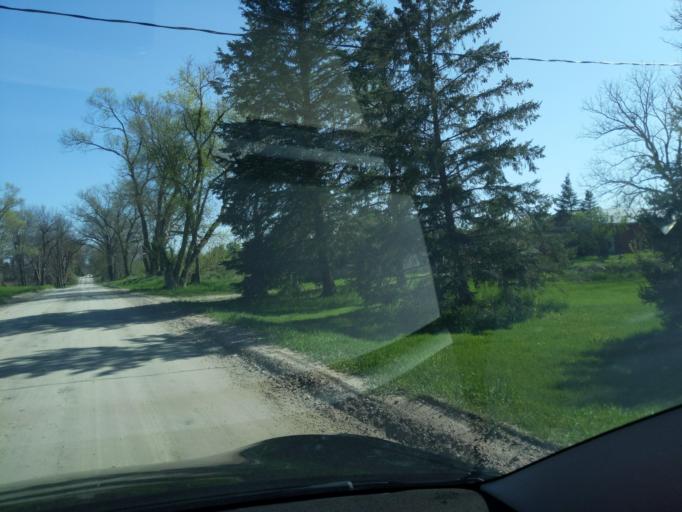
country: US
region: Michigan
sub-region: Ingham County
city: Stockbridge
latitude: 42.4133
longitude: -84.0836
